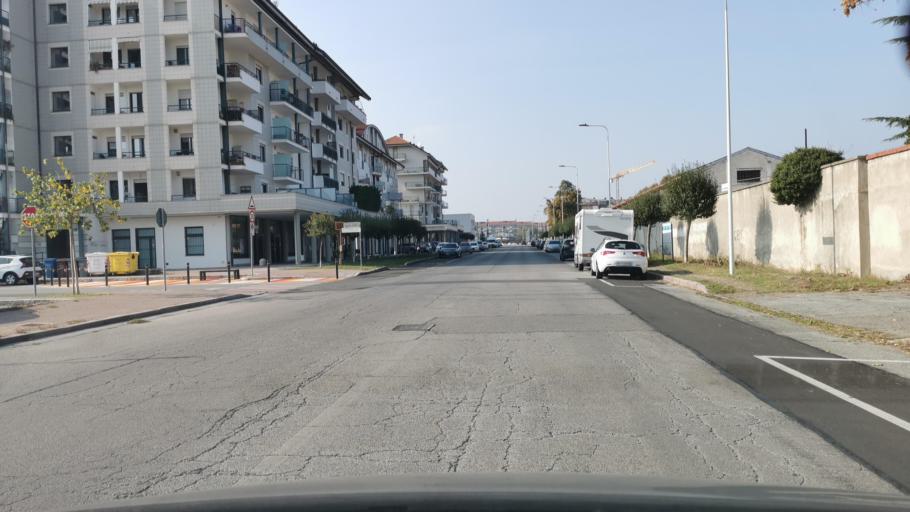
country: IT
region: Piedmont
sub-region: Provincia di Cuneo
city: Cuneo
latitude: 44.3729
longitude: 7.5352
